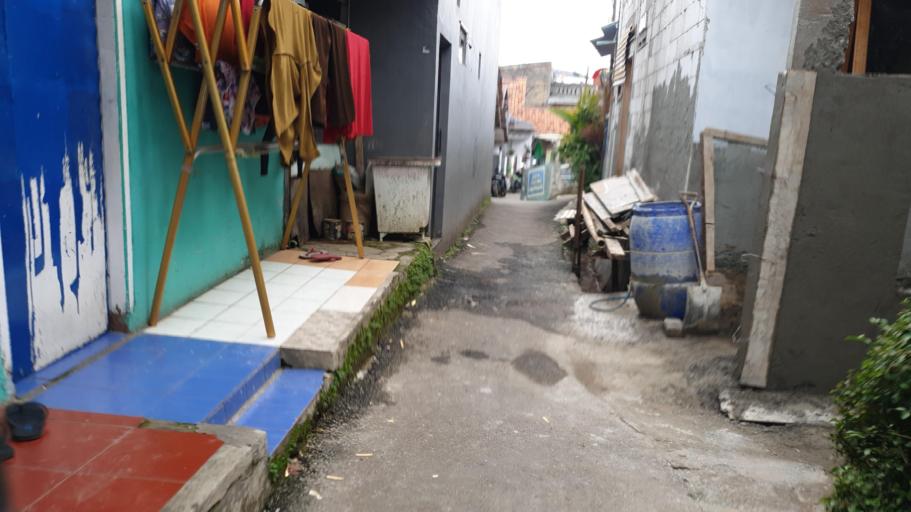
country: ID
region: West Java
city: Depok
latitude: -6.3320
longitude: 106.8215
